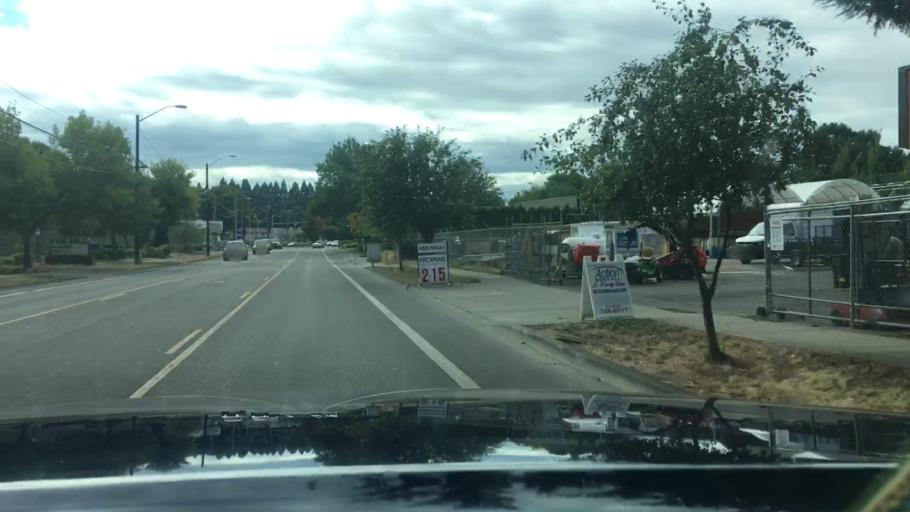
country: US
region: Oregon
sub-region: Lane County
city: Eugene
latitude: 44.0959
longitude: -123.1250
